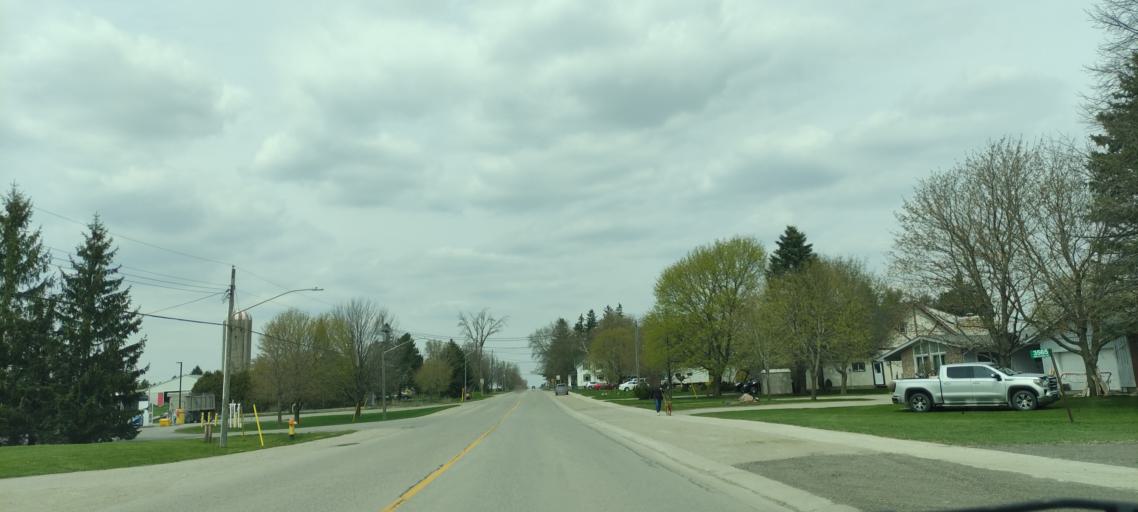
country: CA
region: Ontario
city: Stratford
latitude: 43.3296
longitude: -80.8363
